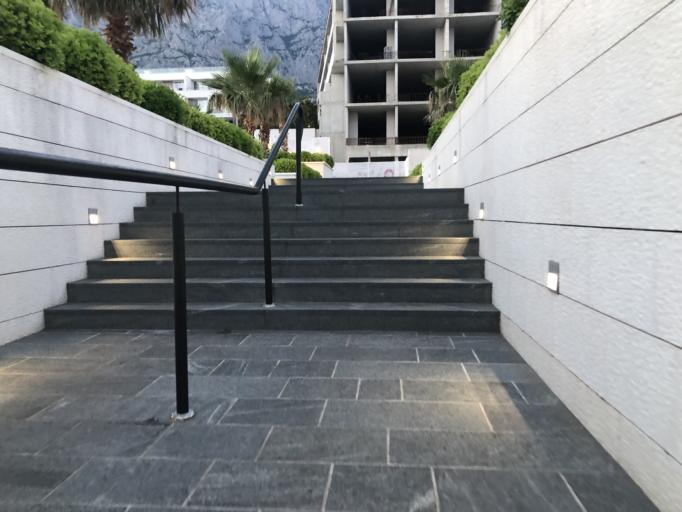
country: HR
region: Splitsko-Dalmatinska
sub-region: Grad Makarska
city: Makarska
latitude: 43.3066
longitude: 17.0019
